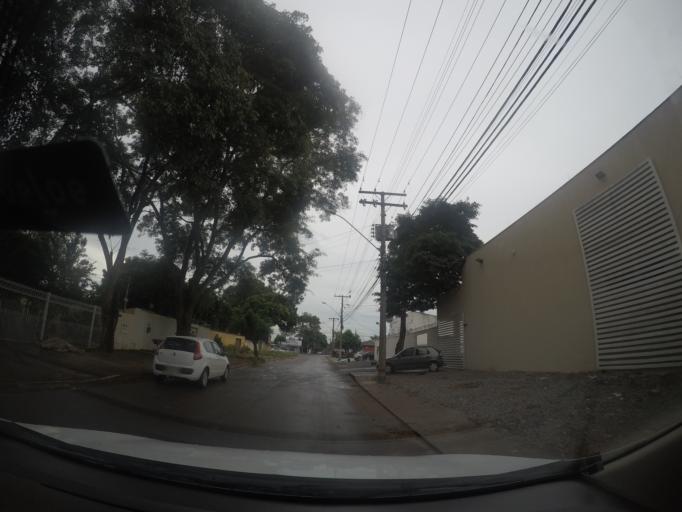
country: BR
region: Goias
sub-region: Goiania
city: Goiania
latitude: -16.6243
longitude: -49.2321
